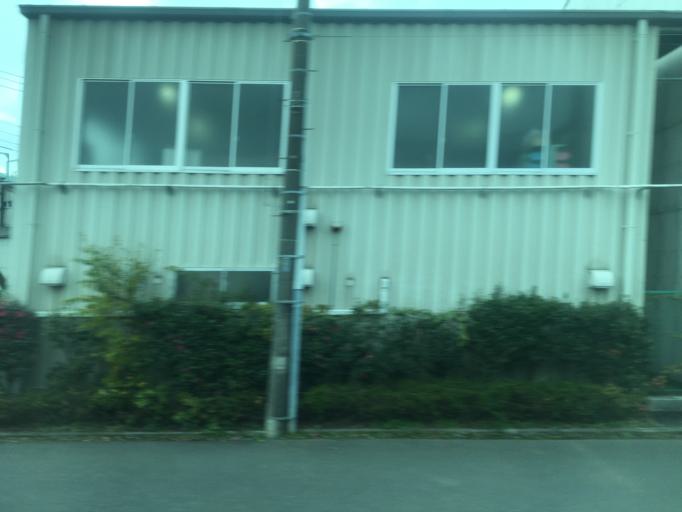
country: JP
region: Saitama
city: Okegawa
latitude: 36.0085
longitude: 139.5536
